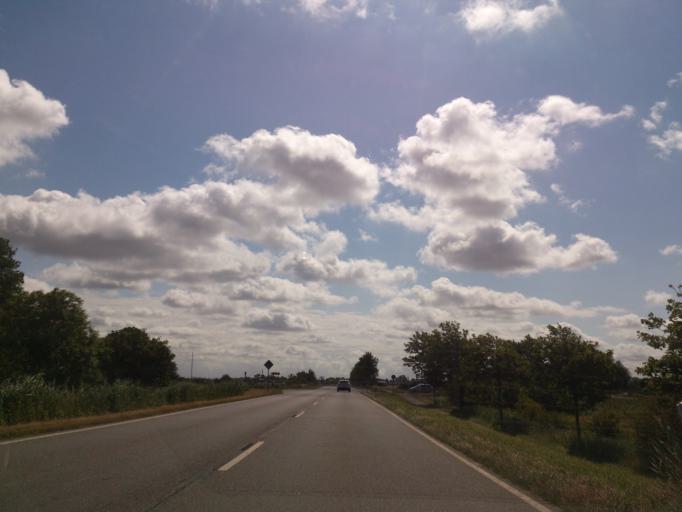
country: DE
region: Schleswig-Holstein
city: Grothusenkoog
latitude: 54.3042
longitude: 8.7616
